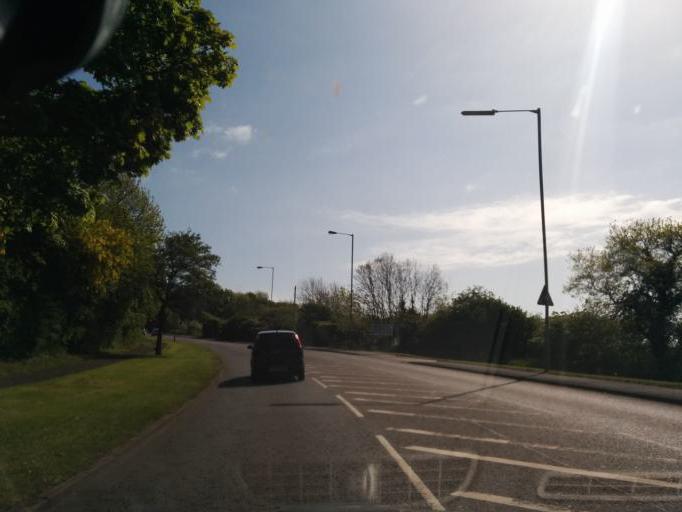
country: GB
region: England
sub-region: Northumberland
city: Ashington
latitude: 55.1672
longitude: -1.5714
